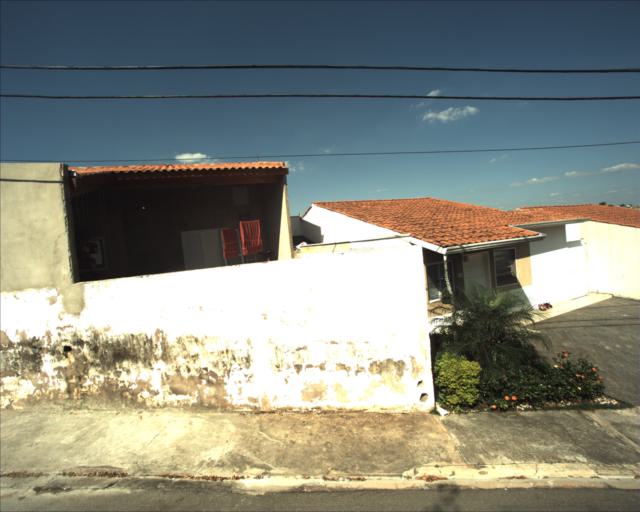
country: BR
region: Sao Paulo
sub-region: Sorocaba
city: Sorocaba
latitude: -23.4555
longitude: -47.5160
